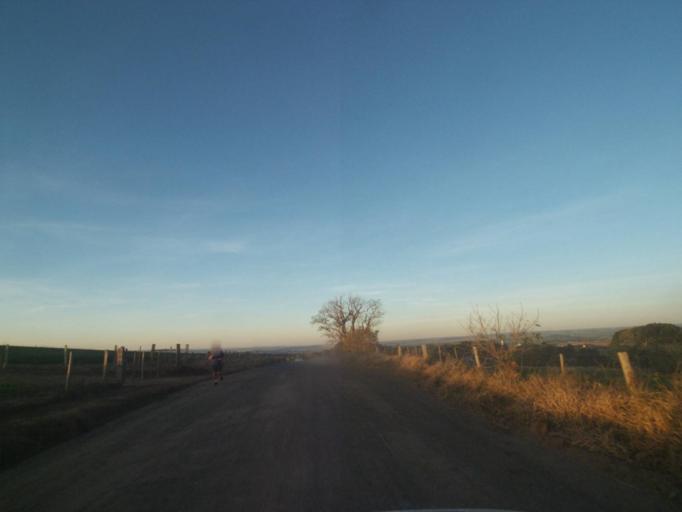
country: BR
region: Parana
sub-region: Tibagi
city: Tibagi
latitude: -24.5274
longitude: -50.4550
